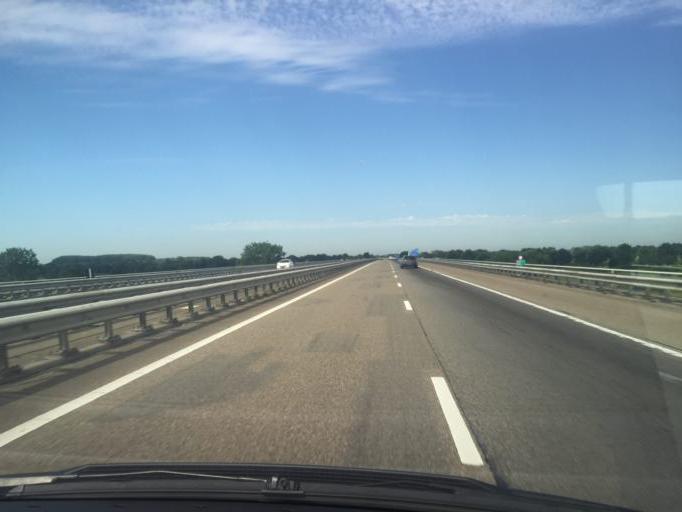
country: NL
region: North Brabant
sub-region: Gemeente Boxmeer
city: Boxmeer
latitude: 51.6638
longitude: 5.9650
